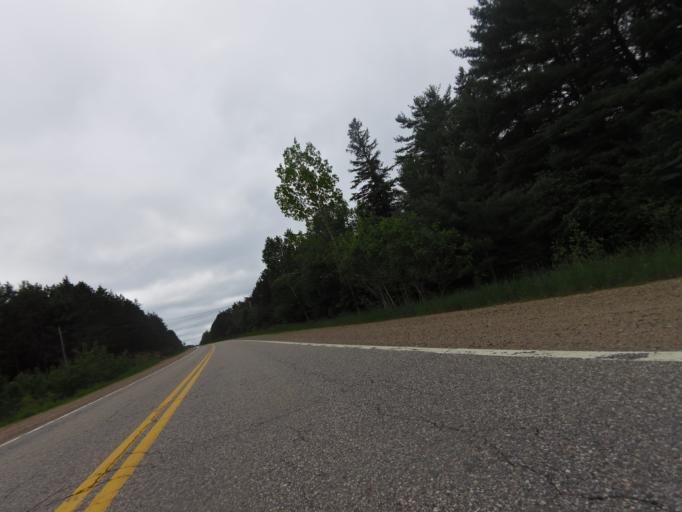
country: CA
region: Quebec
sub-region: Outaouais
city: Shawville
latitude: 45.8718
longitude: -76.4044
